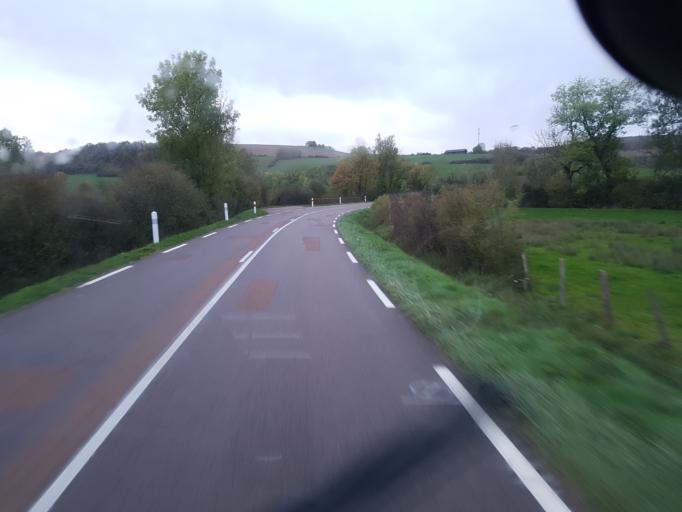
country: FR
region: Bourgogne
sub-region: Departement de la Cote-d'Or
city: Chatillon-sur-Seine
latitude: 47.6967
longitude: 4.6175
